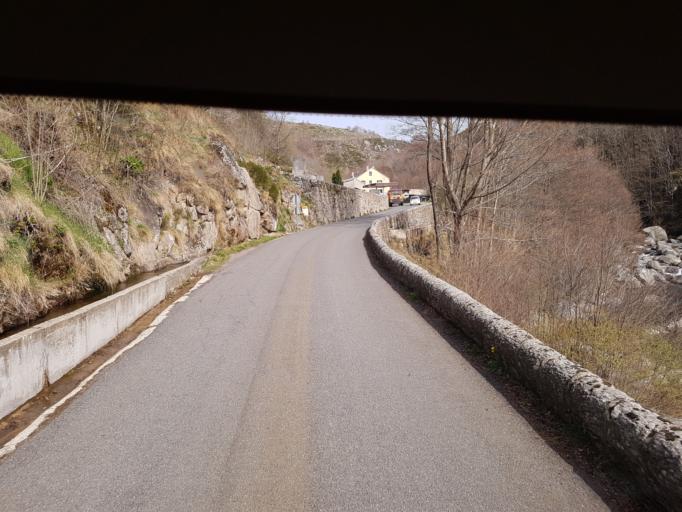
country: FR
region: Languedoc-Roussillon
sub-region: Departement de la Lozere
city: Florac
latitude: 44.3633
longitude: 3.7484
